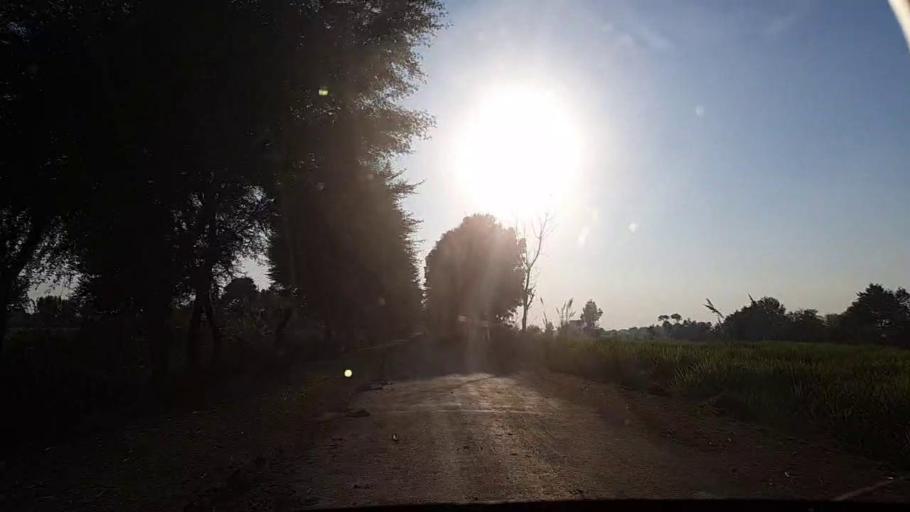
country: PK
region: Sindh
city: Sobhadero
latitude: 27.4152
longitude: 68.3997
